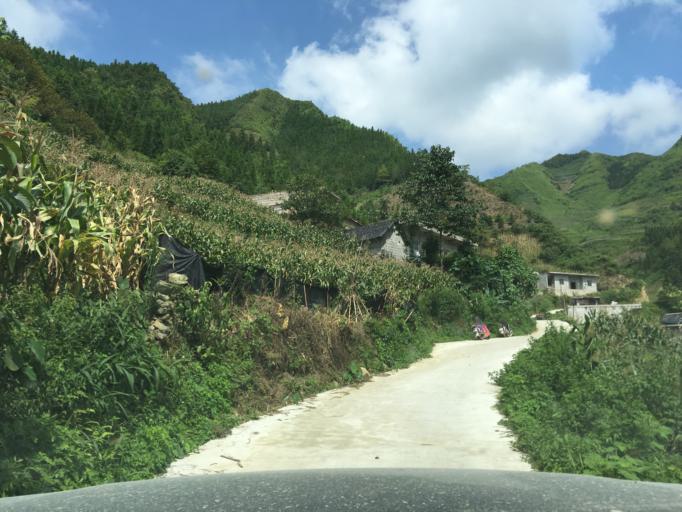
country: CN
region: Guangxi Zhuangzu Zizhiqu
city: Xinzhou
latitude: 24.9675
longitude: 105.6203
